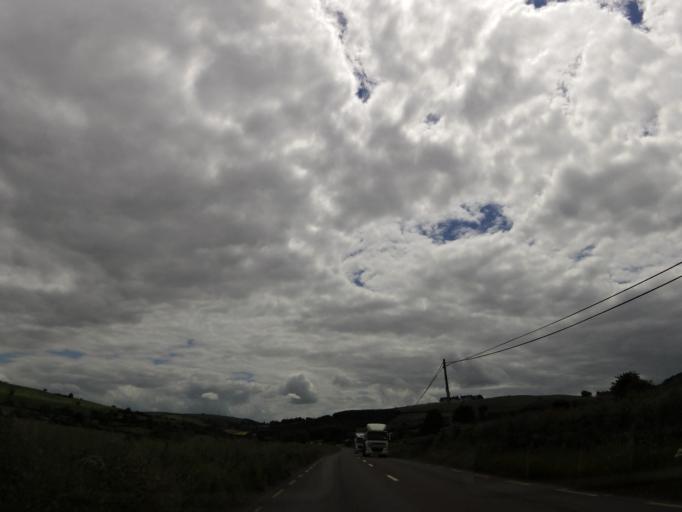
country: IE
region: Munster
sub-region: North Tipperary
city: Templemore
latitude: 52.7608
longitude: -8.0141
